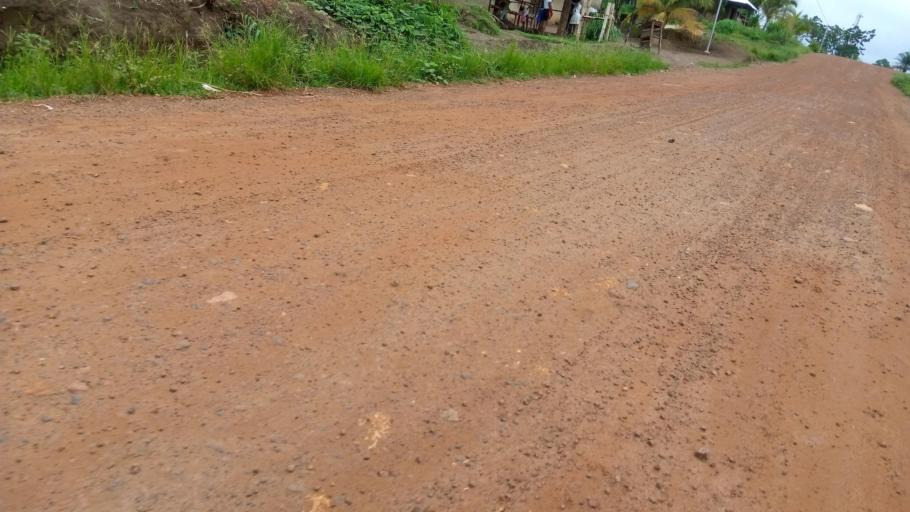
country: SL
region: Southern Province
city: Gandorhun
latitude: 7.4395
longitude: -11.8405
